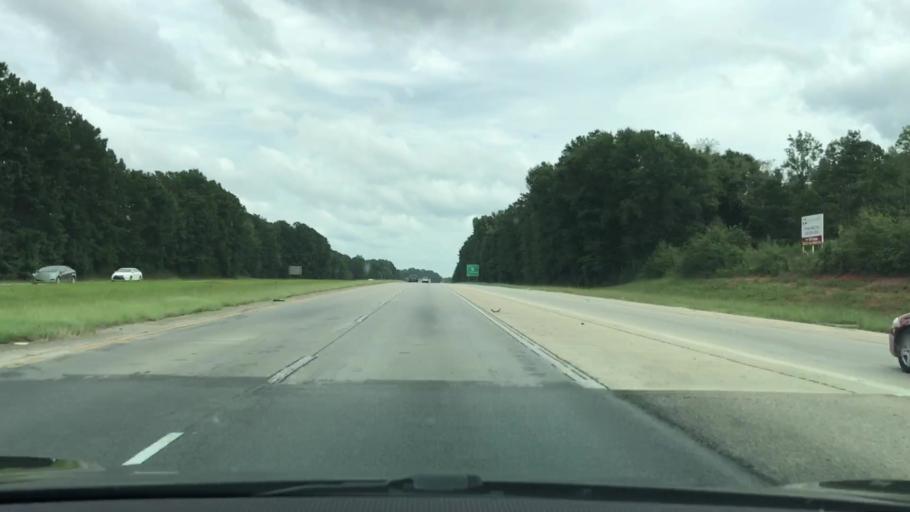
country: US
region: Georgia
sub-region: Troup County
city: La Grange
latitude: 32.9918
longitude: -85.0251
